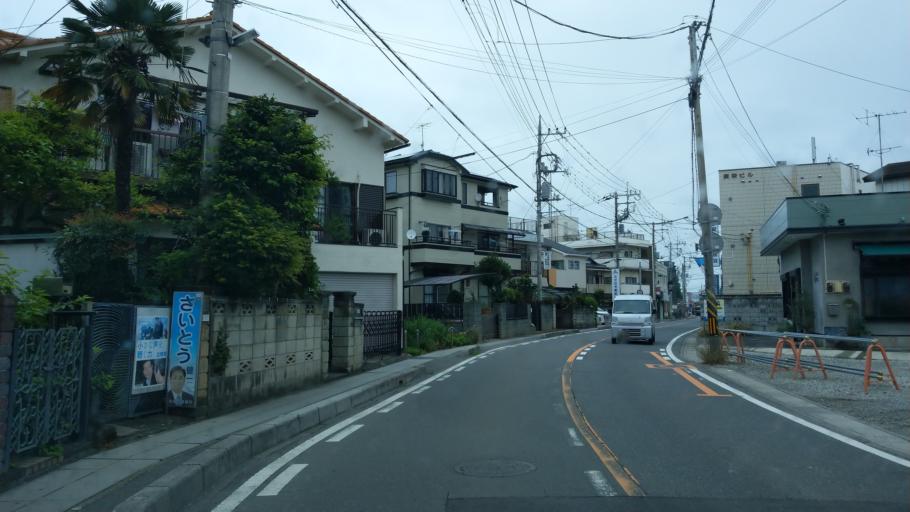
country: JP
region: Saitama
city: Saitama
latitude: 35.9303
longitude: 139.6508
